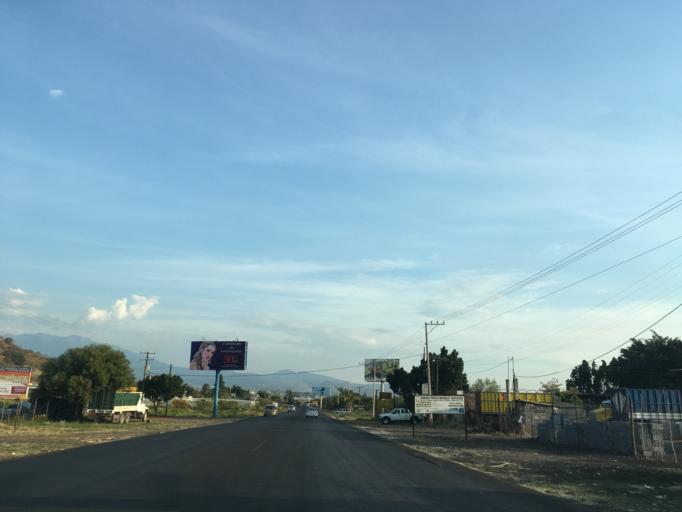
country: MX
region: Michoacan
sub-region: Los Reyes
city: La Higuerita (Colonia San Rafael)
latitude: 19.6262
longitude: -102.4882
